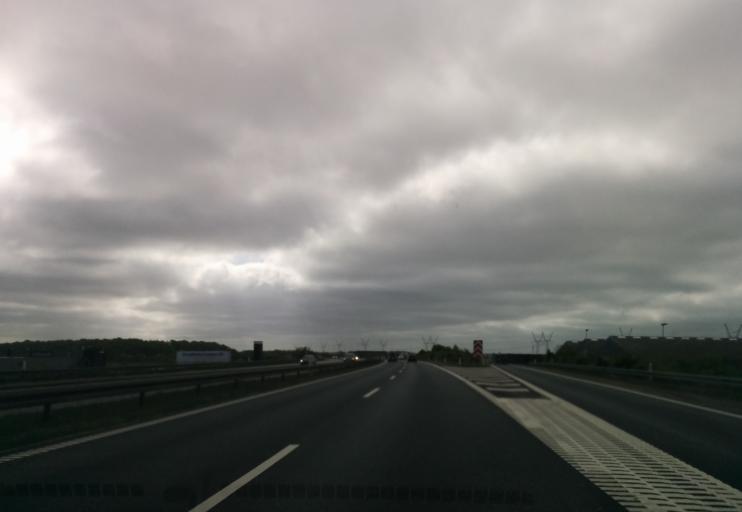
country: DK
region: South Denmark
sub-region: Fredericia Kommune
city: Taulov
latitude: 55.5466
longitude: 9.6431
